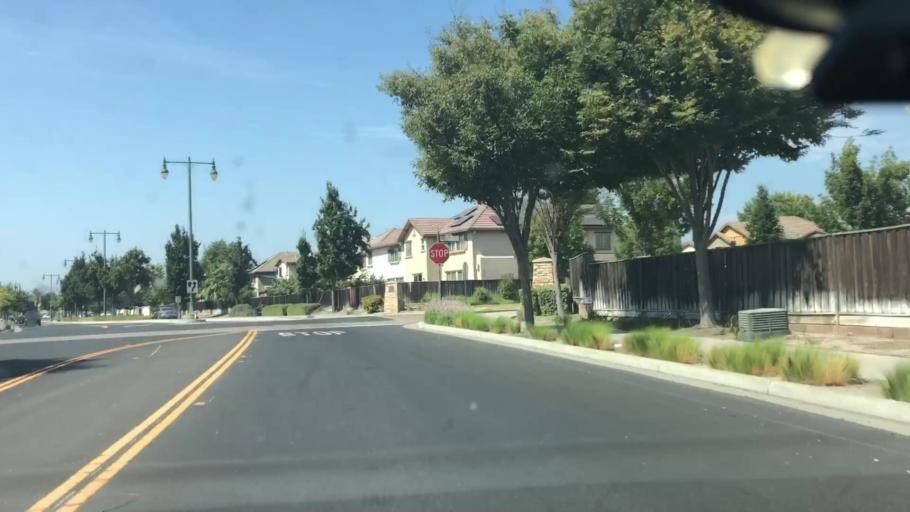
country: US
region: California
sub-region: San Joaquin County
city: Lathrop
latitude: 37.8082
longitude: -121.3044
